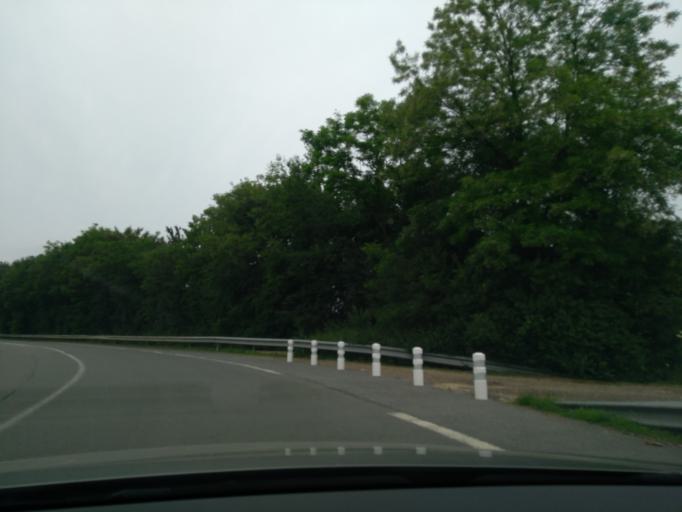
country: FR
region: Picardie
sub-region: Departement de l'Aisne
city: Athies-sous-Laon
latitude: 49.6074
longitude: 3.6642
